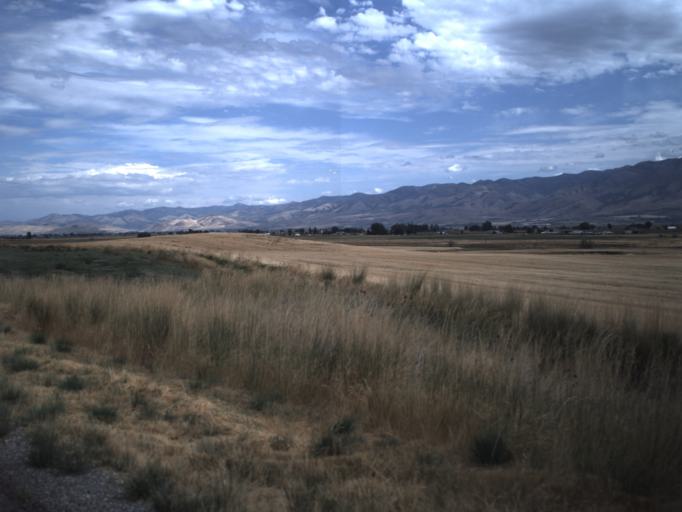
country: US
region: Utah
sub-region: Cache County
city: Benson
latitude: 41.8852
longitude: -111.9511
